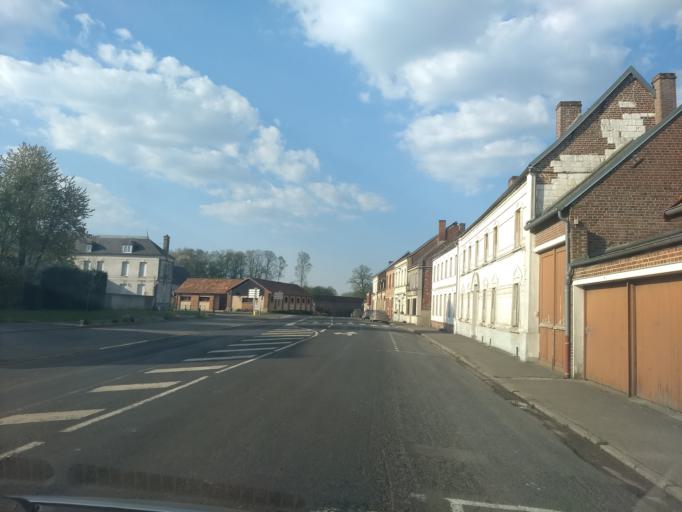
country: FR
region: Picardie
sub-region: Departement de la Somme
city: Albert
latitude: 50.0790
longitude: 2.6023
